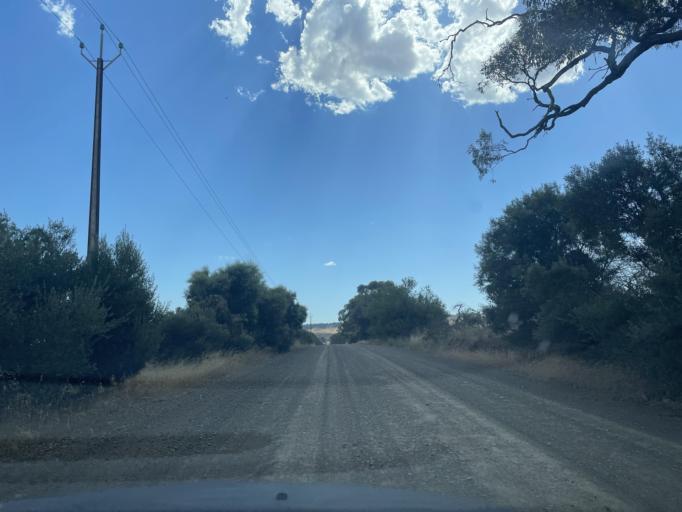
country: AU
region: South Australia
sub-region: Clare and Gilbert Valleys
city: Clare
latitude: -33.9097
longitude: 138.7320
